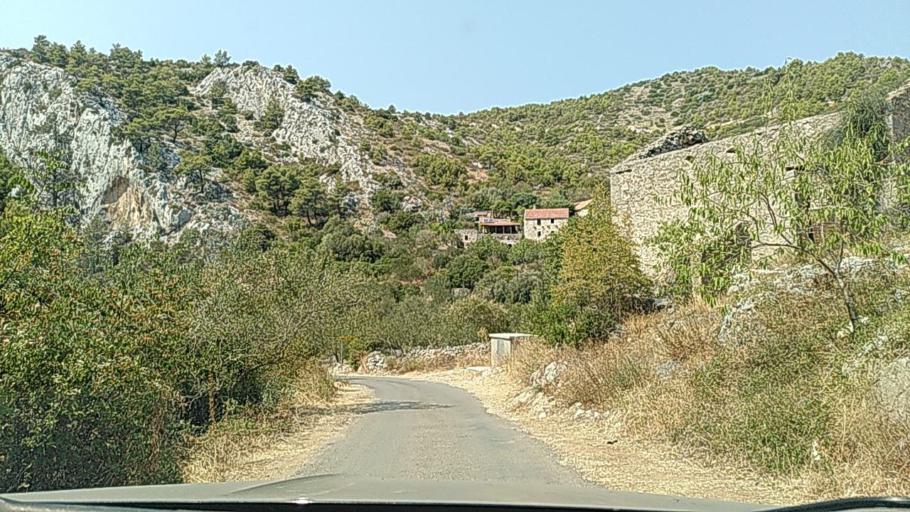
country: HR
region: Splitsko-Dalmatinska
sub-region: Grad Hvar
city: Hvar
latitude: 43.1676
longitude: 16.5035
